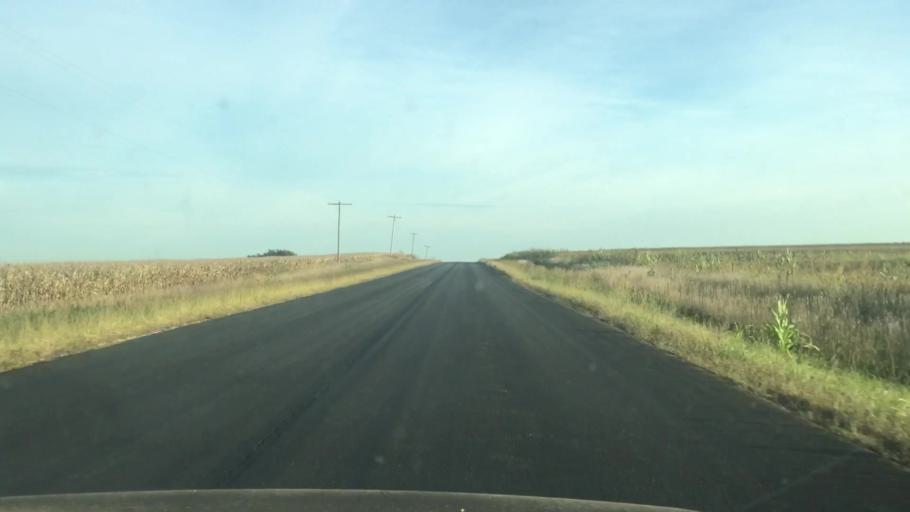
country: US
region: Kansas
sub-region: Marshall County
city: Marysville
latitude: 39.8903
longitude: -96.6010
